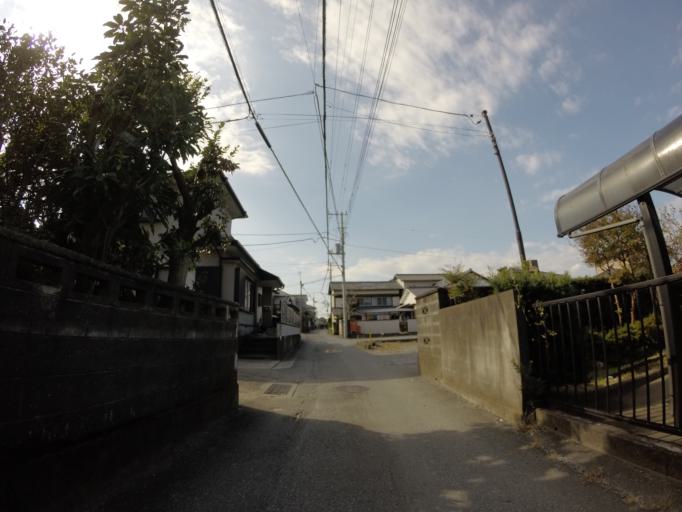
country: JP
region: Shizuoka
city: Fuji
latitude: 35.1352
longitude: 138.6817
